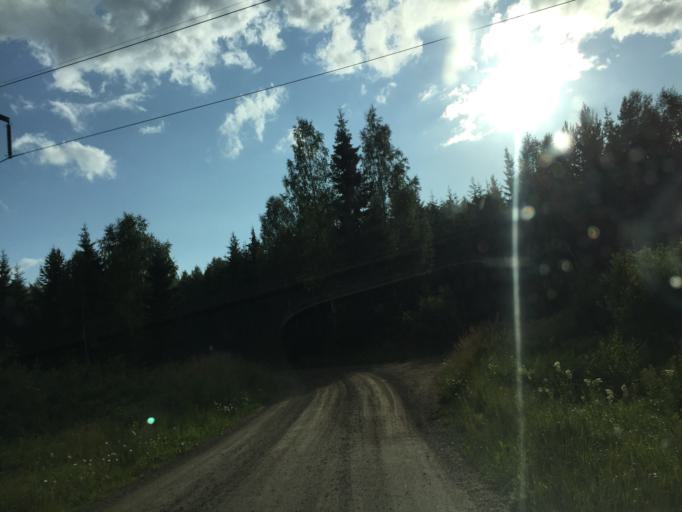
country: SE
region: OEstergoetland
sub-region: Motala Kommun
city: Ryd
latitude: 58.7009
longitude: 15.0331
